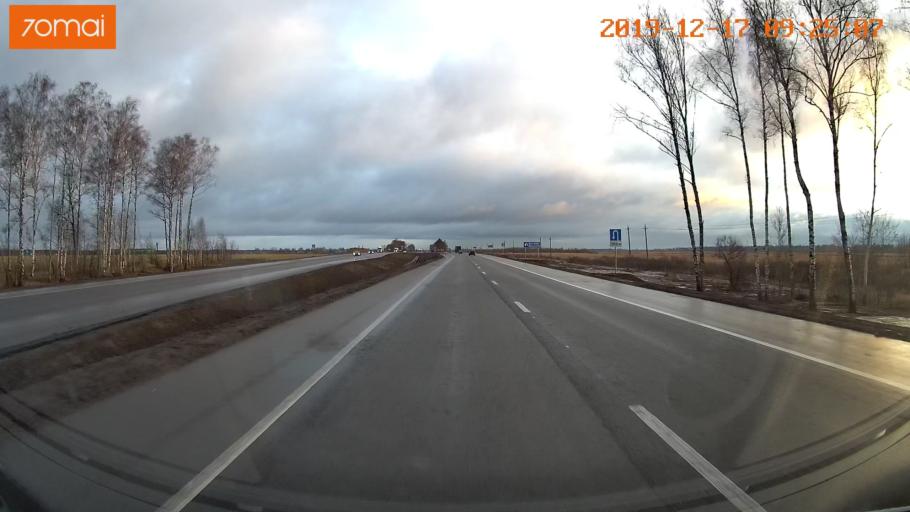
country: RU
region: Vladimir
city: Vorsha
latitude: 56.0405
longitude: 40.0475
